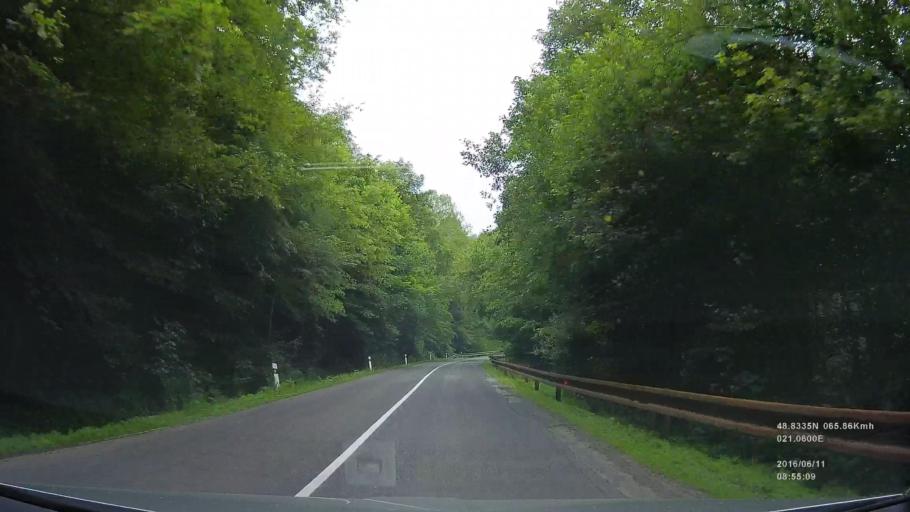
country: SK
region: Kosicky
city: Gelnica
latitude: 48.8347
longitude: 21.0685
